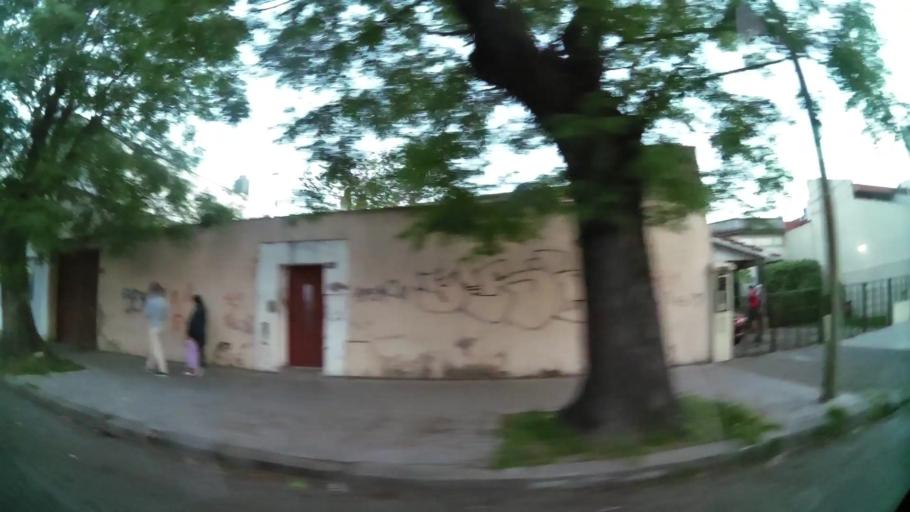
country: AR
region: Buenos Aires F.D.
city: Villa Lugano
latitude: -34.6763
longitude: -58.4731
